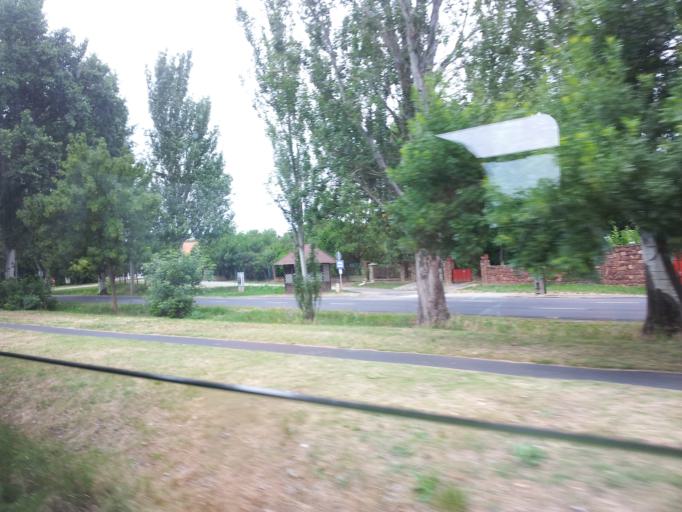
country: HU
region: Veszprem
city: Revfueloep
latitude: 46.8240
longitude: 17.6160
